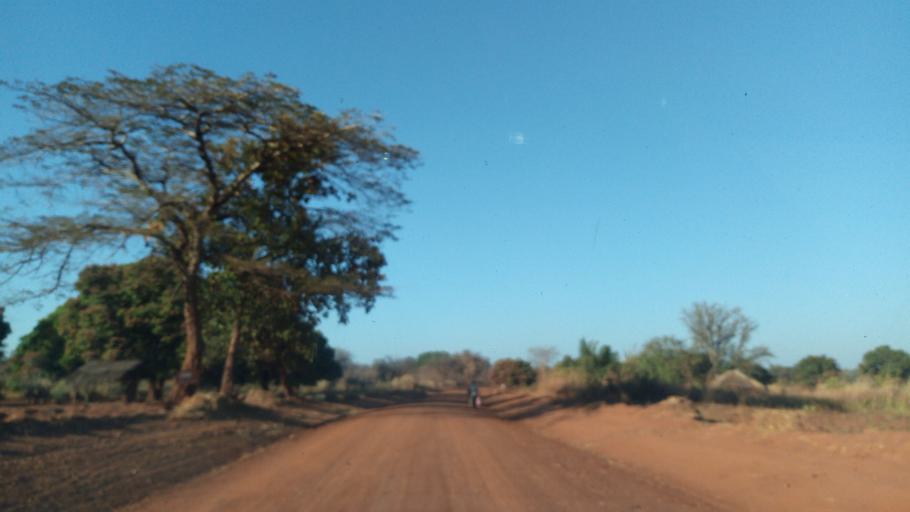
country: ZM
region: Luapula
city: Mwense
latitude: -10.4246
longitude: 28.6014
